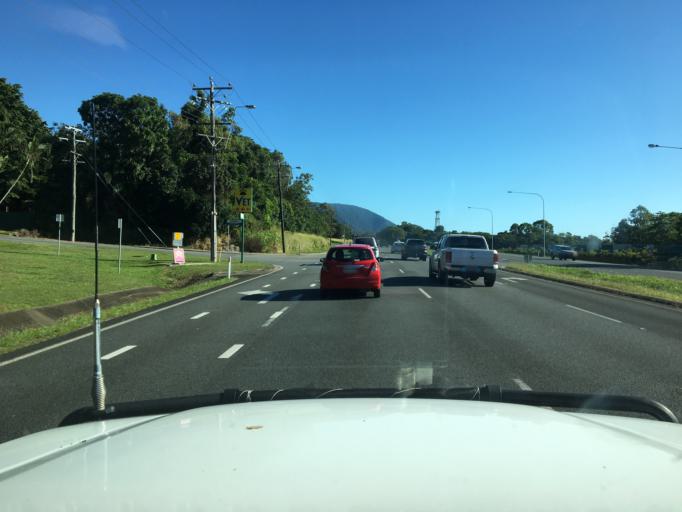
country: AU
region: Queensland
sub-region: Cairns
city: Trinity Beach
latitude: -16.8056
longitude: 145.6904
